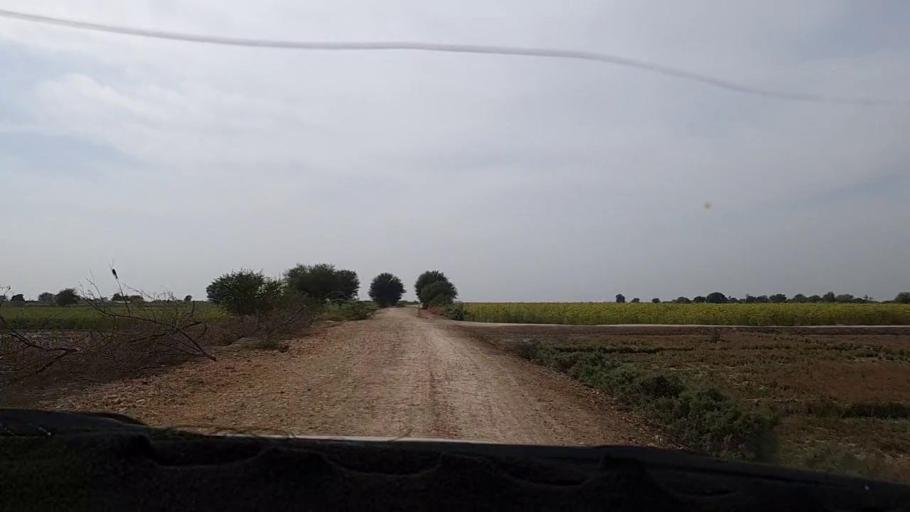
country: PK
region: Sindh
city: Pithoro
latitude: 25.5534
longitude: 69.3533
